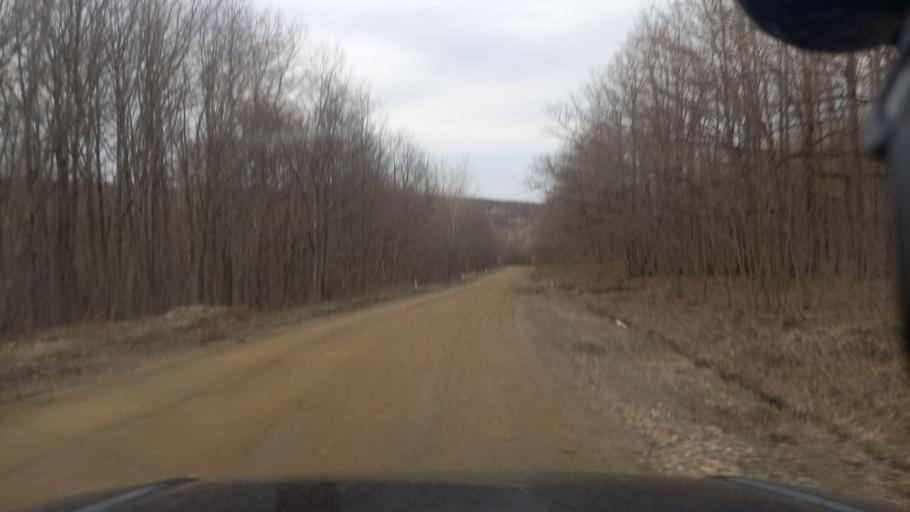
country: RU
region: Krasnodarskiy
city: Goryachiy Klyuch
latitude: 44.7011
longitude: 39.0171
